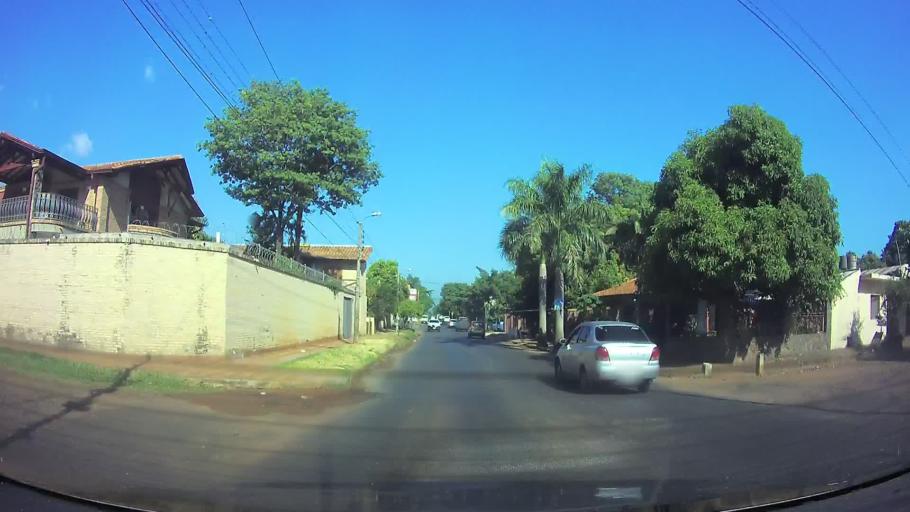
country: PY
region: Central
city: San Lorenzo
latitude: -25.2760
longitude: -57.5022
